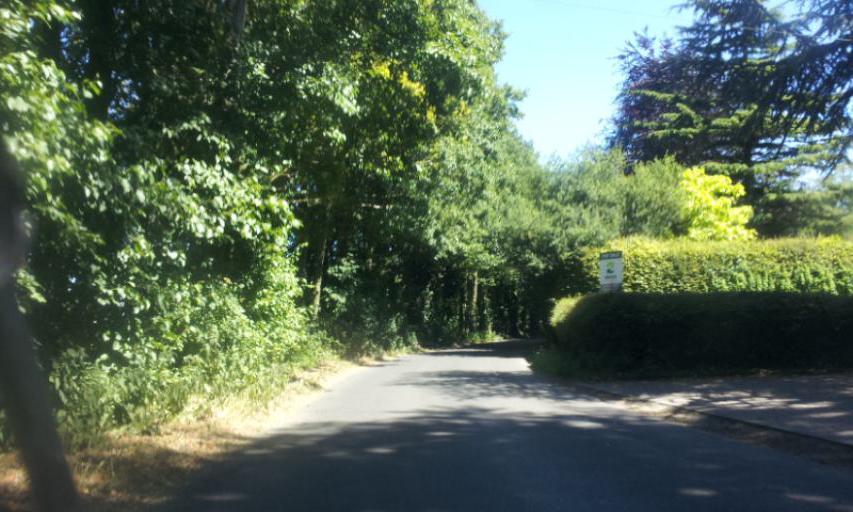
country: GB
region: England
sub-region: Kent
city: Sittingbourne
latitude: 51.3045
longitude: 0.7159
